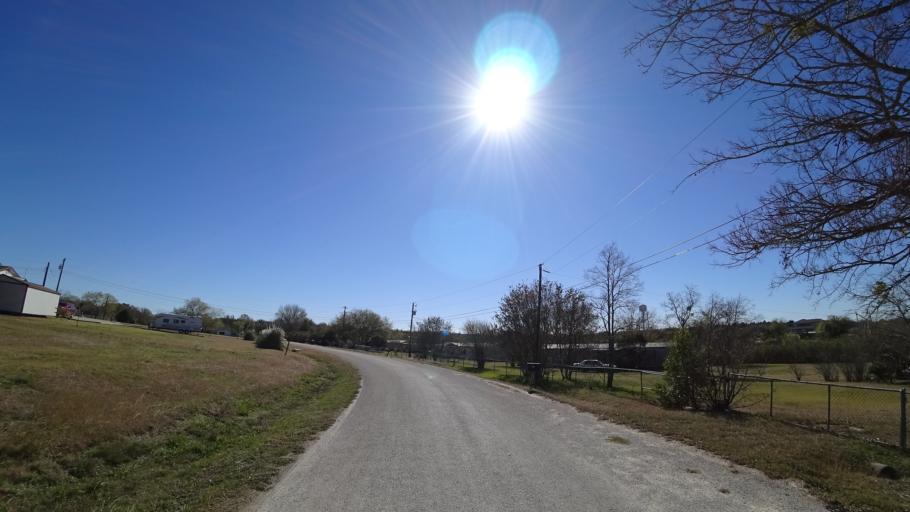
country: US
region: Texas
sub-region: Travis County
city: Garfield
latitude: 30.1041
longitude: -97.5974
